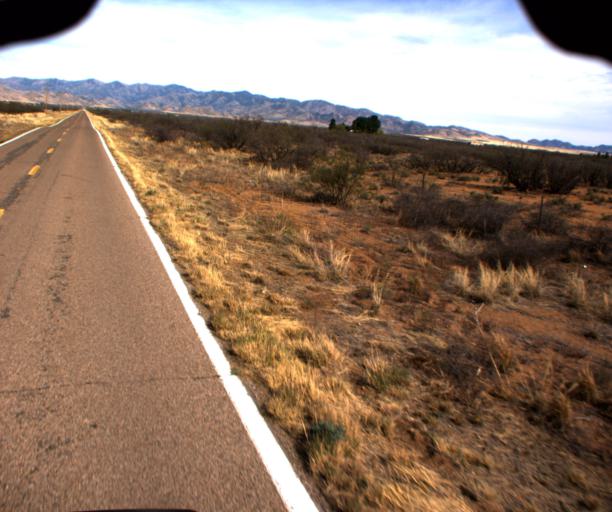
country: US
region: Arizona
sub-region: Cochise County
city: Willcox
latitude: 31.8760
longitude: -109.5506
